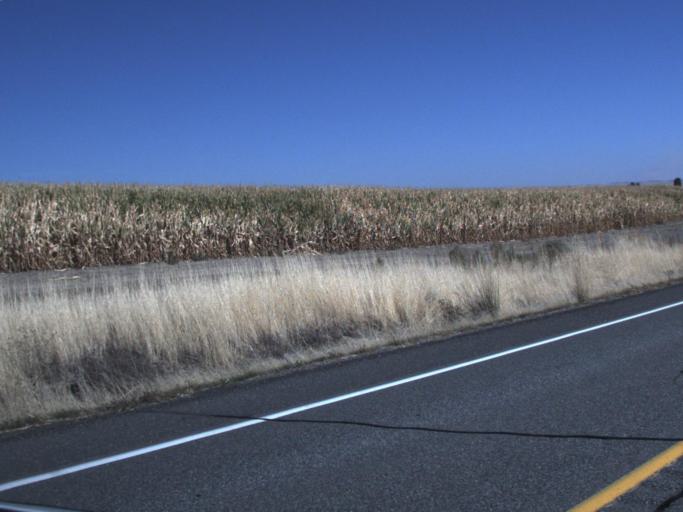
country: US
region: Washington
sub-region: Walla Walla County
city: Garrett
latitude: 46.2970
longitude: -118.6644
